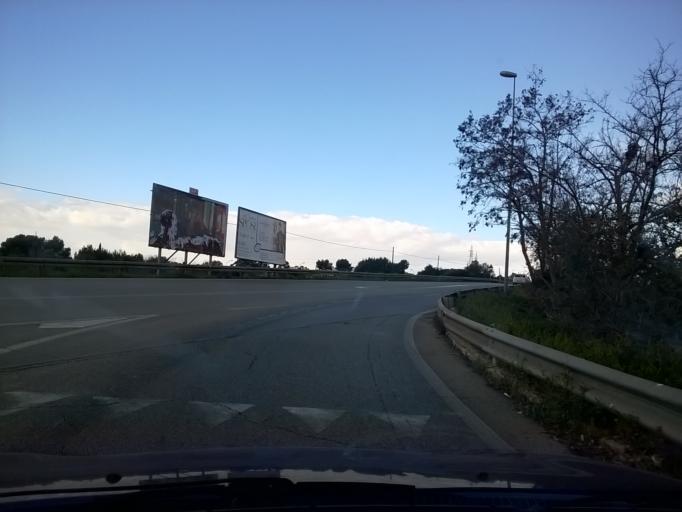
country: IT
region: Apulia
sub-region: Provincia di Taranto
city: Paolo VI
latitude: 40.5108
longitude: 17.2910
